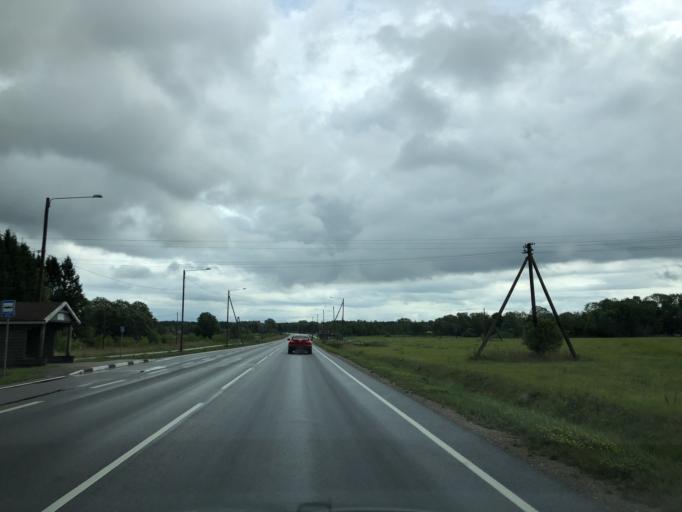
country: EE
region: Laeaene
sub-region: Ridala Parish
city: Uuemoisa
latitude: 58.9725
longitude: 23.8625
